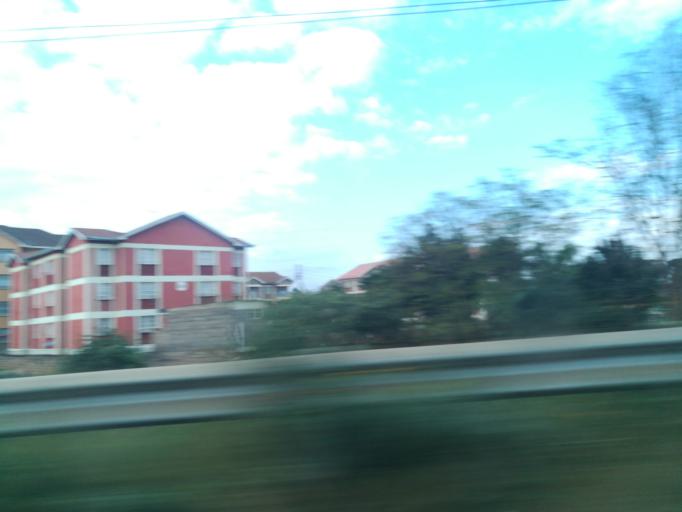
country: KE
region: Nairobi Area
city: Thika
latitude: -1.0404
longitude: 37.0636
